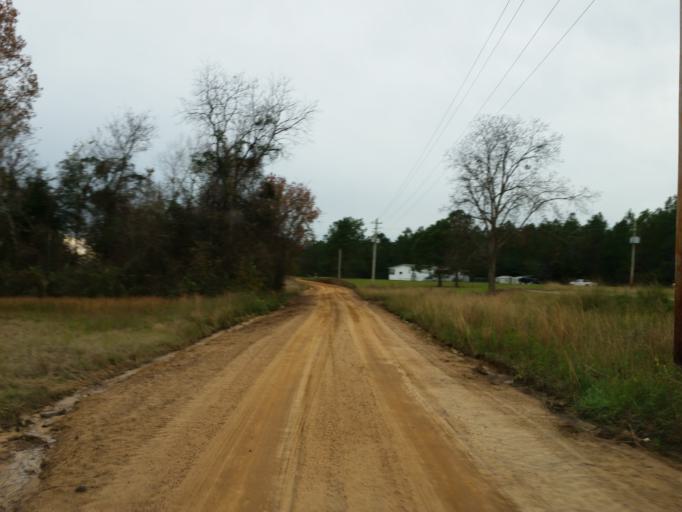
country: US
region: Georgia
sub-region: Crisp County
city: Cordele
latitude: 31.9040
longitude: -83.7107
